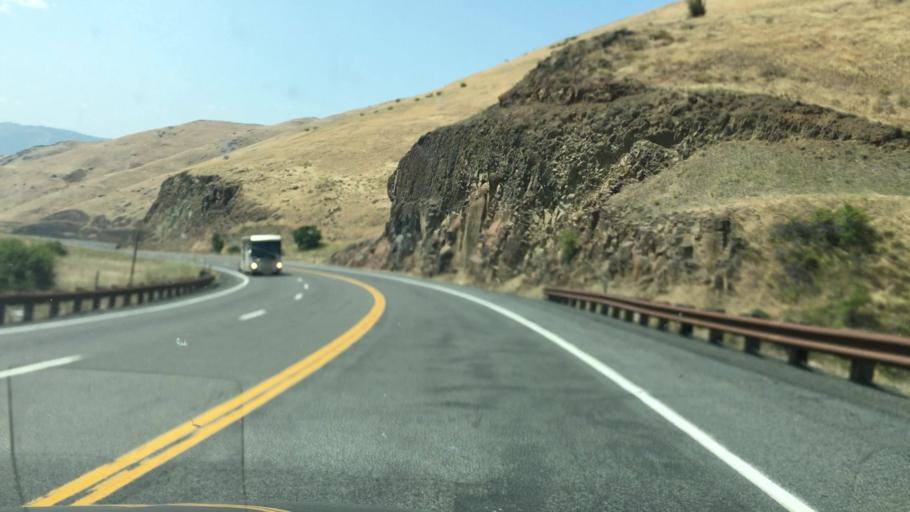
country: US
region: Idaho
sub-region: Idaho County
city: Grangeville
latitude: 45.8230
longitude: -116.2644
